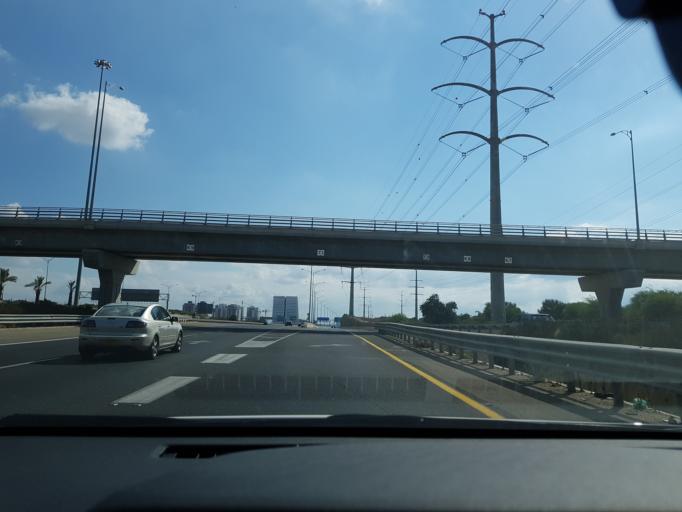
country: IL
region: Central District
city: Rishon LeZiyyon
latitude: 31.9519
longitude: 34.7887
